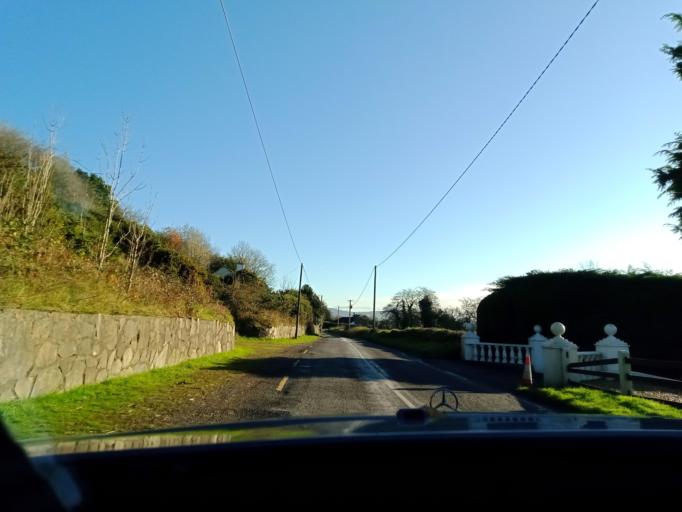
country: IE
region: Leinster
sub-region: Kilkenny
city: Piltown
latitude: 52.3945
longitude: -7.3610
